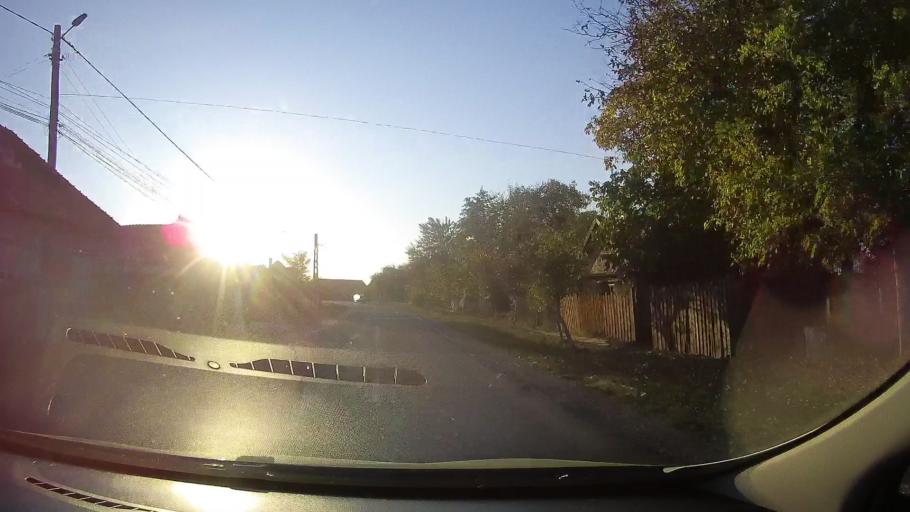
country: RO
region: Bihor
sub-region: Comuna Salard
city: Salard
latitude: 47.2209
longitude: 22.0402
